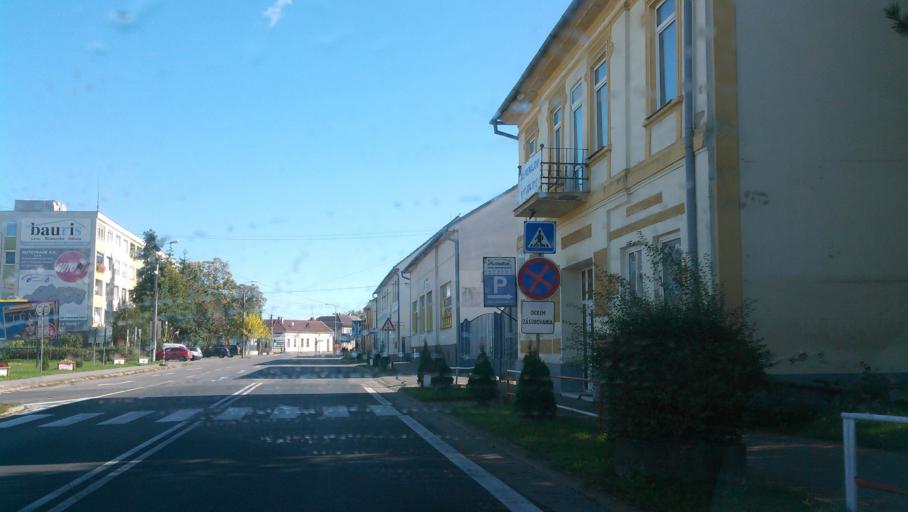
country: SK
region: Banskobystricky
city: Rimavska Sobota
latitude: 48.3810
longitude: 20.0200
